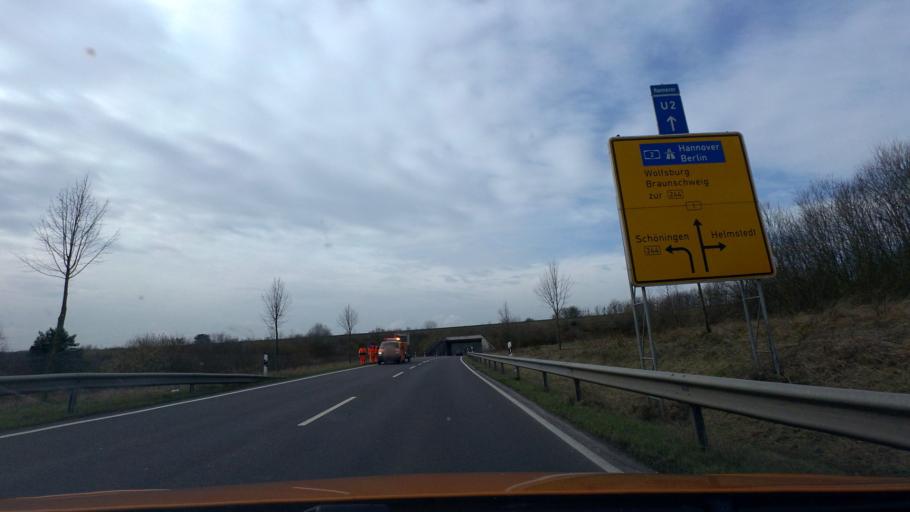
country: DE
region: Lower Saxony
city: Helmstedt
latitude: 52.2152
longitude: 11.0048
